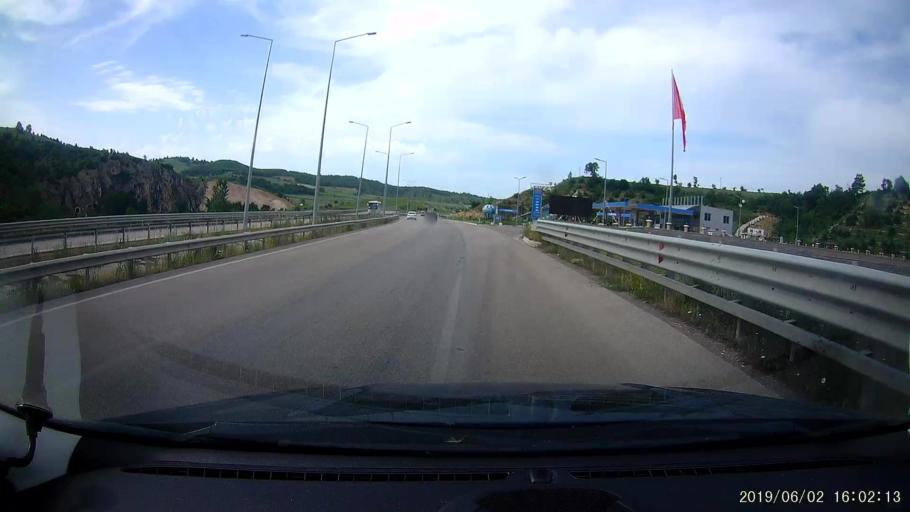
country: TR
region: Samsun
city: Havza
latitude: 40.9409
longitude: 35.6588
